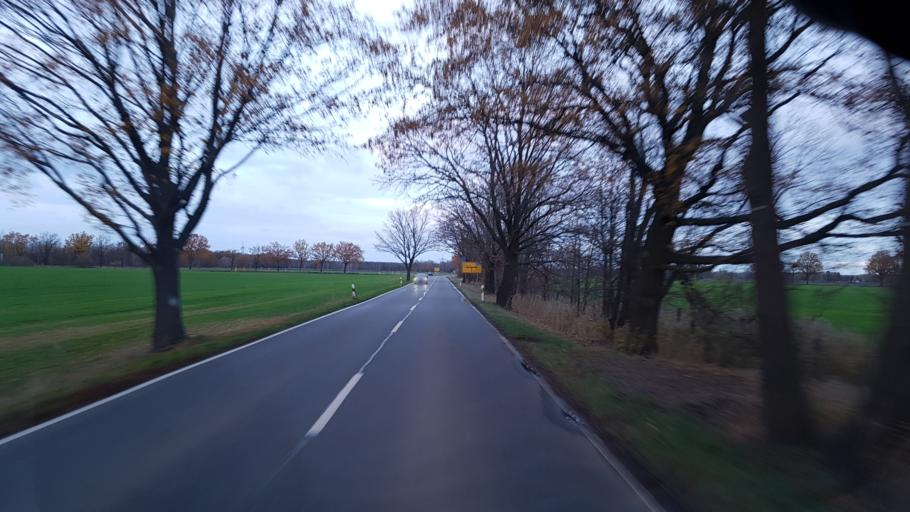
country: DE
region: Brandenburg
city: Schraden
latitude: 51.4635
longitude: 13.7123
